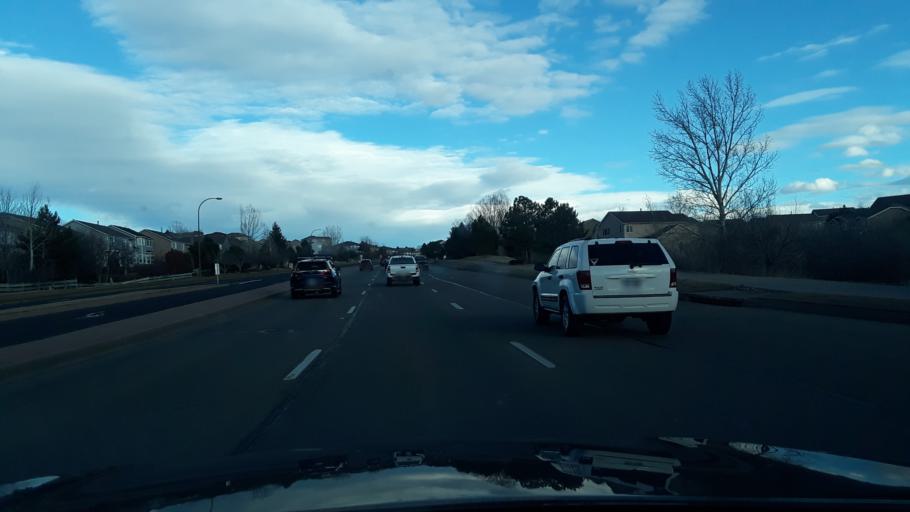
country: US
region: Colorado
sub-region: El Paso County
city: Gleneagle
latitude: 39.0083
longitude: -104.8039
